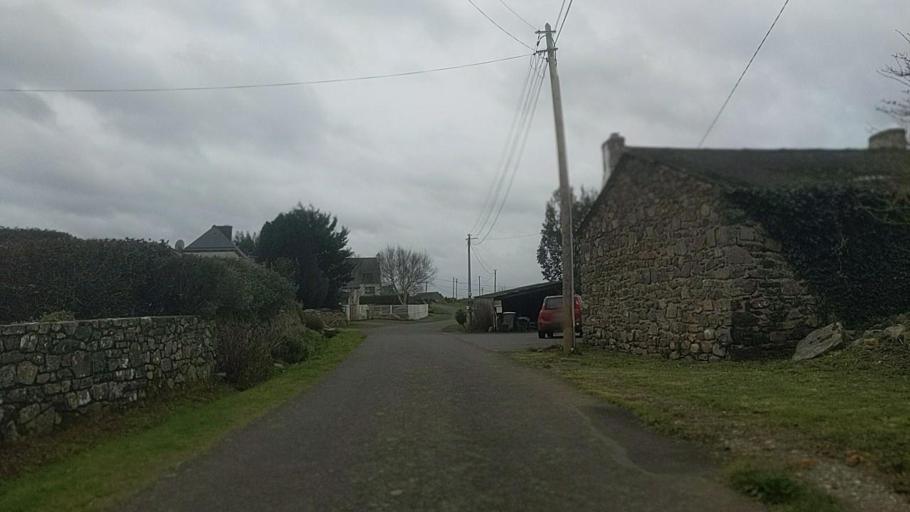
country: FR
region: Brittany
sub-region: Departement des Cotes-d'Armor
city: Tredarzec
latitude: 48.8229
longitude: -3.1931
